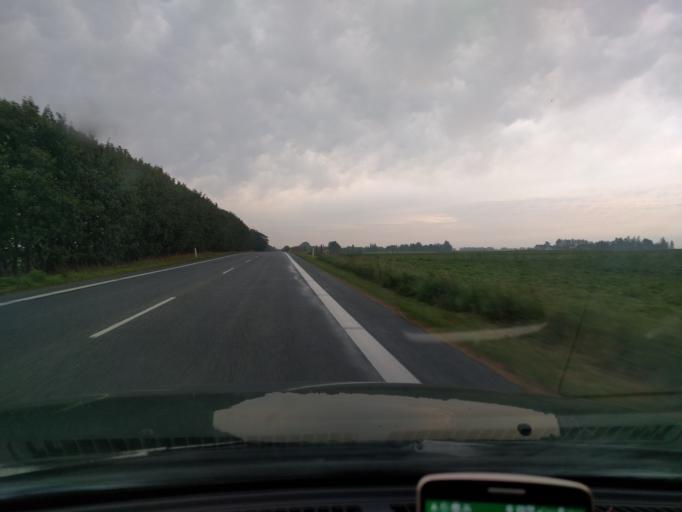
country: DK
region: Zealand
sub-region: Guldborgsund Kommune
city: Norre Alslev
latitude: 54.9083
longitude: 11.8755
